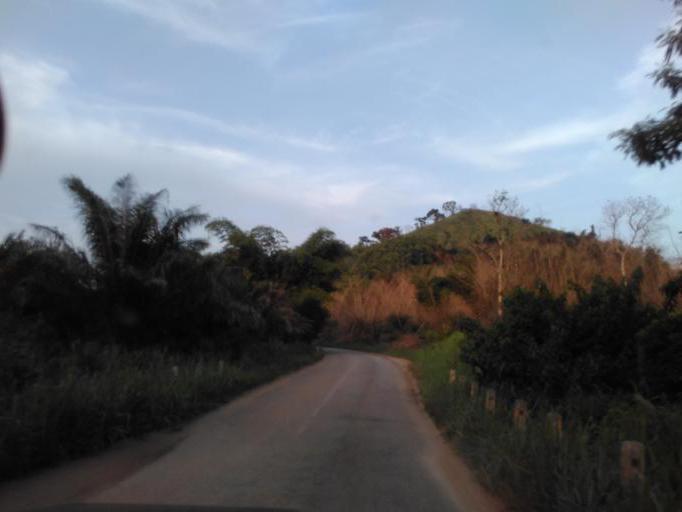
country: GH
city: Bekwai
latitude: 6.5507
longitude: -1.4347
